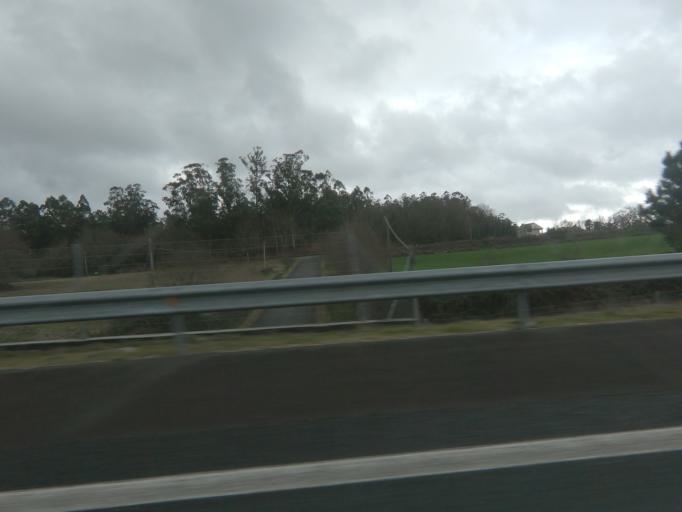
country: ES
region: Galicia
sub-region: Provincia da Coruna
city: Vedra
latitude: 42.8100
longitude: -8.4814
